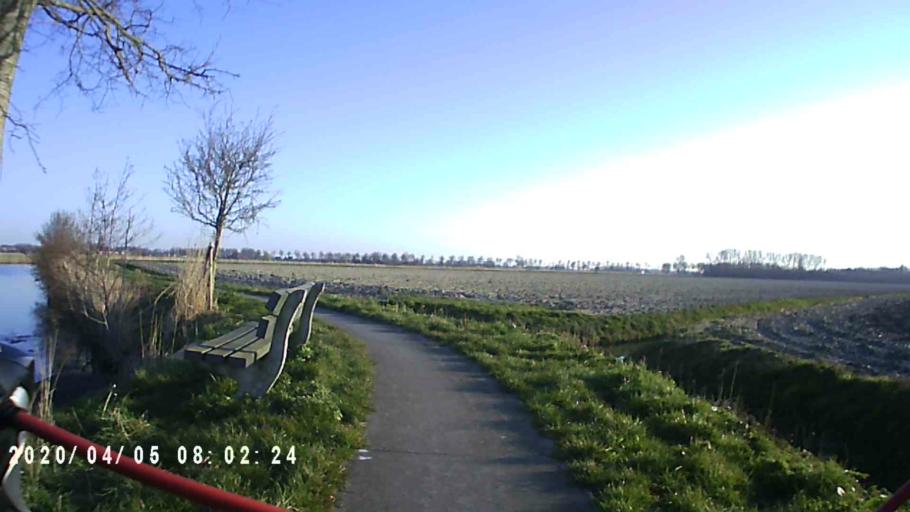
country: NL
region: Groningen
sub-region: Gemeente Zuidhorn
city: Oldehove
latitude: 53.3471
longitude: 6.4354
